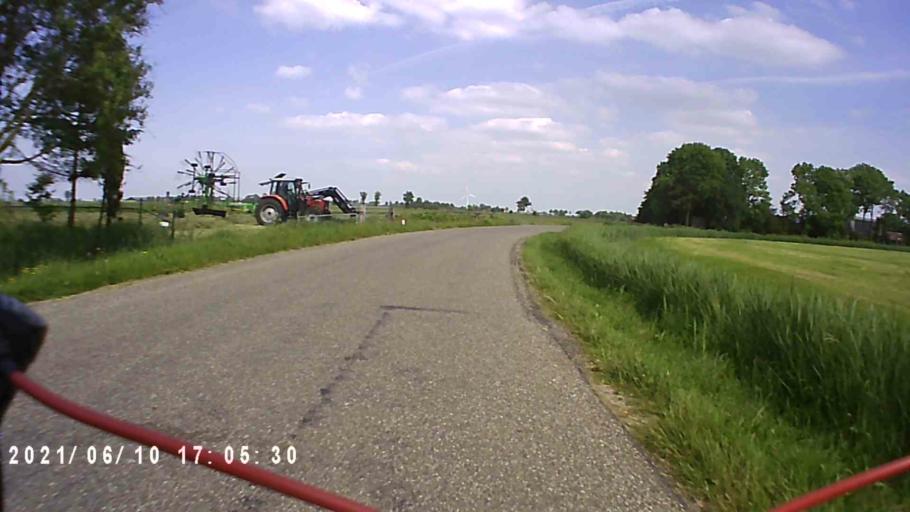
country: NL
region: Friesland
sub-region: Gemeente Kollumerland en Nieuwkruisland
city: Kollum
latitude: 53.2811
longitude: 6.1689
